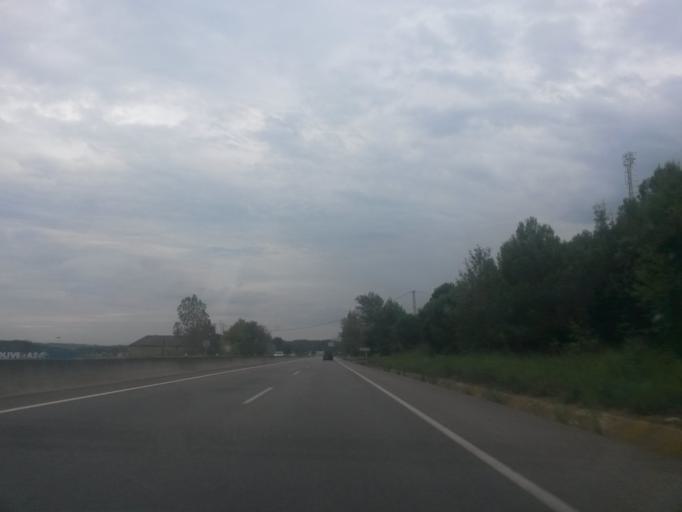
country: ES
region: Catalonia
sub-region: Provincia de Girona
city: Cornella del Terri
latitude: 42.0881
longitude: 2.8111
